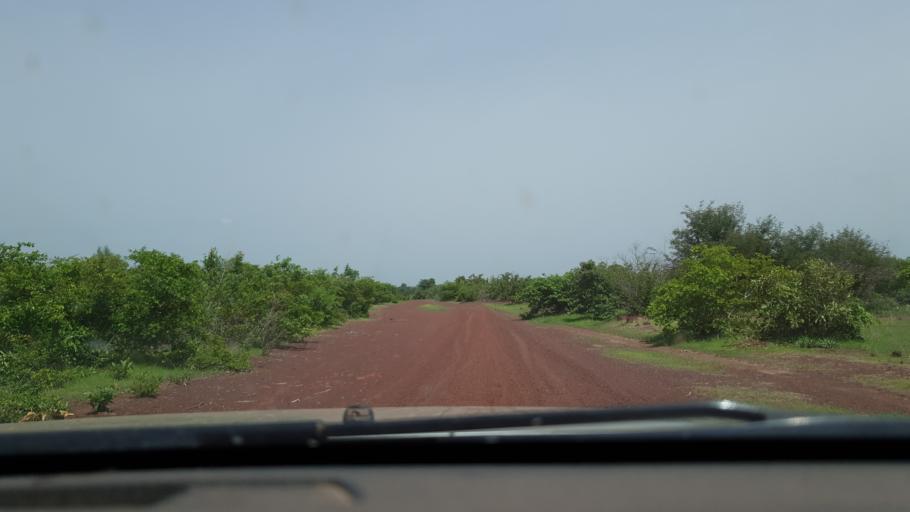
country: ML
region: Koulikoro
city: Koulikoro
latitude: 12.6662
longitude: -7.2330
